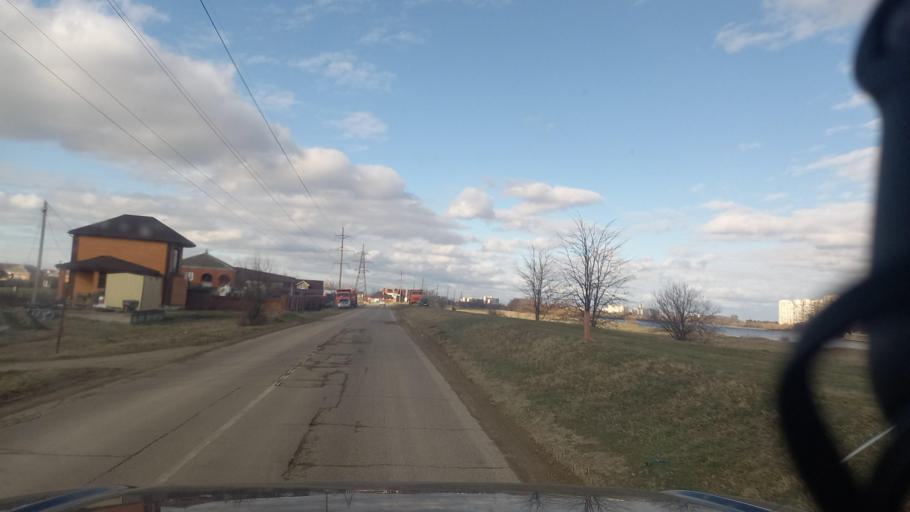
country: RU
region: Adygeya
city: Yablonovskiy
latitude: 45.0271
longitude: 38.8976
